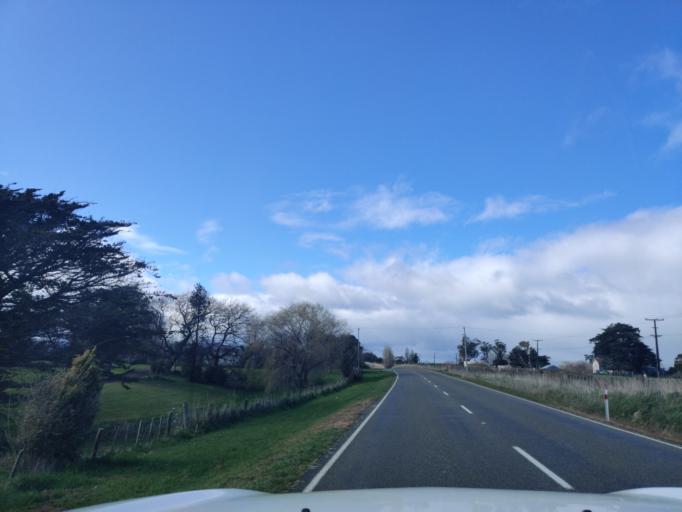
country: NZ
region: Manawatu-Wanganui
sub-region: Palmerston North City
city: Palmerston North
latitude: -40.2876
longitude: 175.6763
